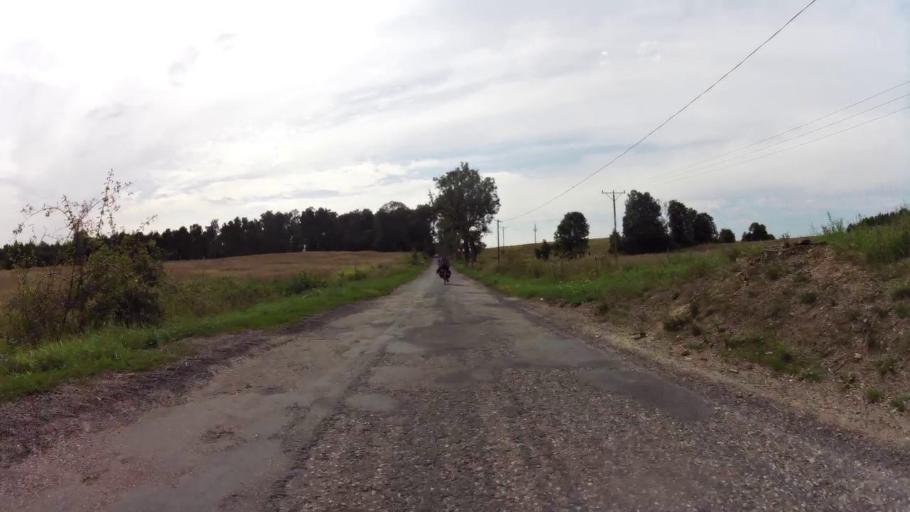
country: PL
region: West Pomeranian Voivodeship
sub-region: Powiat lobeski
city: Wegorzyno
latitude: 53.5425
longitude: 15.5949
